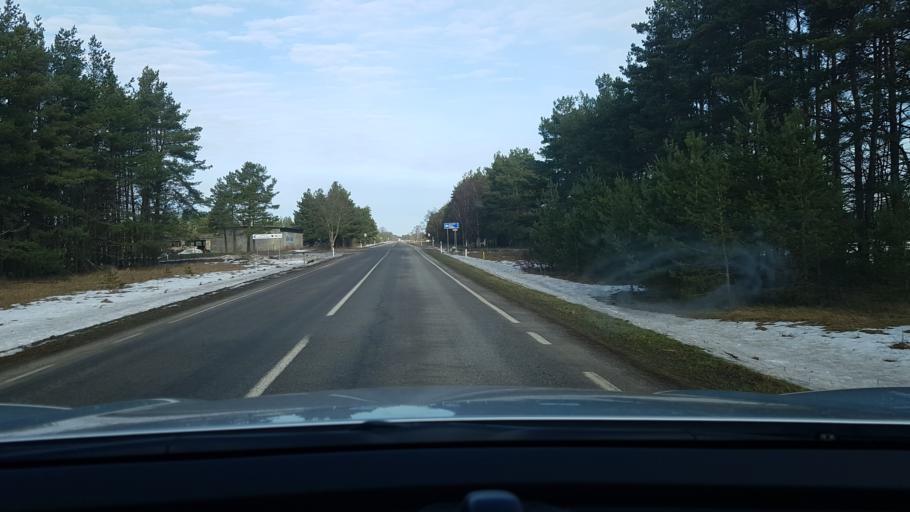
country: EE
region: Saare
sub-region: Kuressaare linn
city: Kuressaare
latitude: 58.5127
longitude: 22.7053
